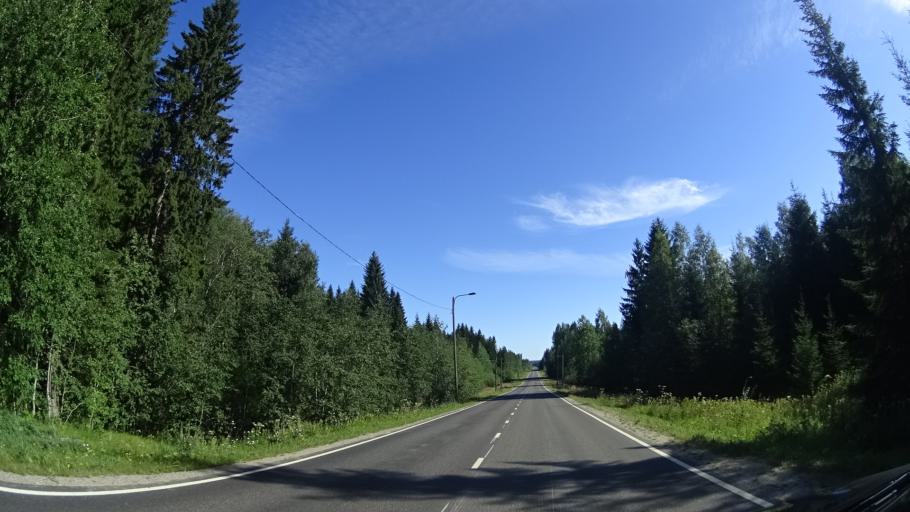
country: FI
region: Central Finland
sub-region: Jyvaeskylae
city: Uurainen
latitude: 62.4264
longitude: 25.3750
